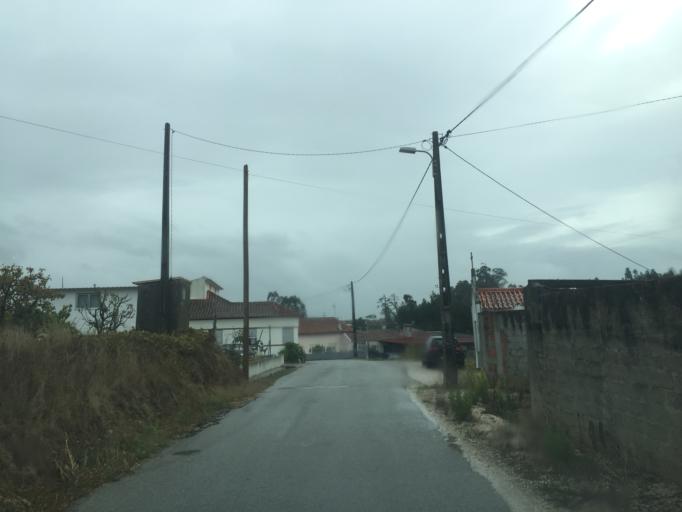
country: PT
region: Coimbra
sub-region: Figueira da Foz
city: Lavos
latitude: 40.0657
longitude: -8.7784
